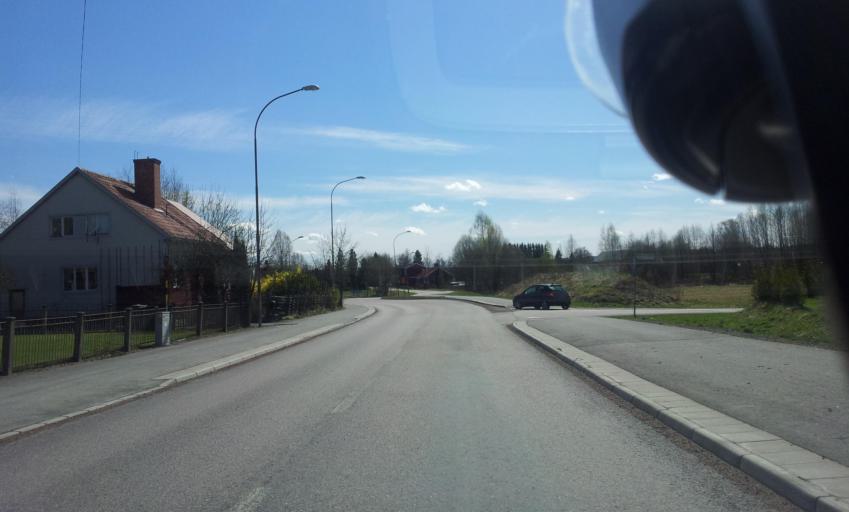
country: SE
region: Dalarna
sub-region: Borlange Kommun
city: Borlaenge
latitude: 60.4840
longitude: 15.4656
